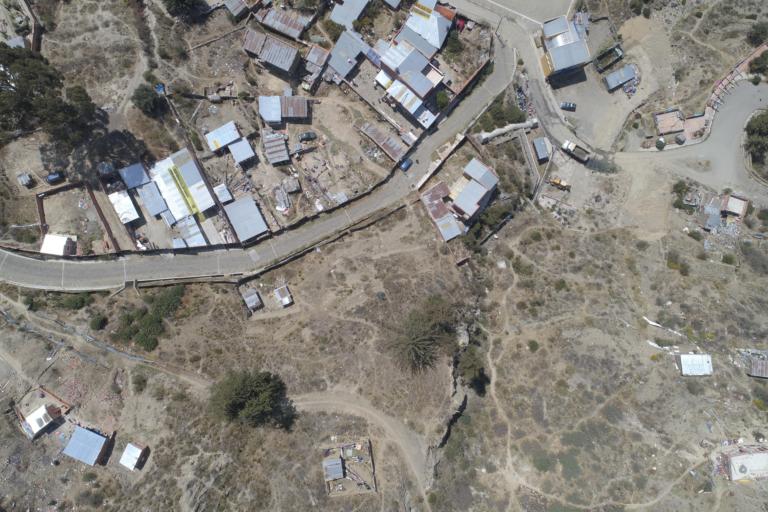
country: BO
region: La Paz
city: La Paz
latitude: -16.5000
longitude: -68.0998
